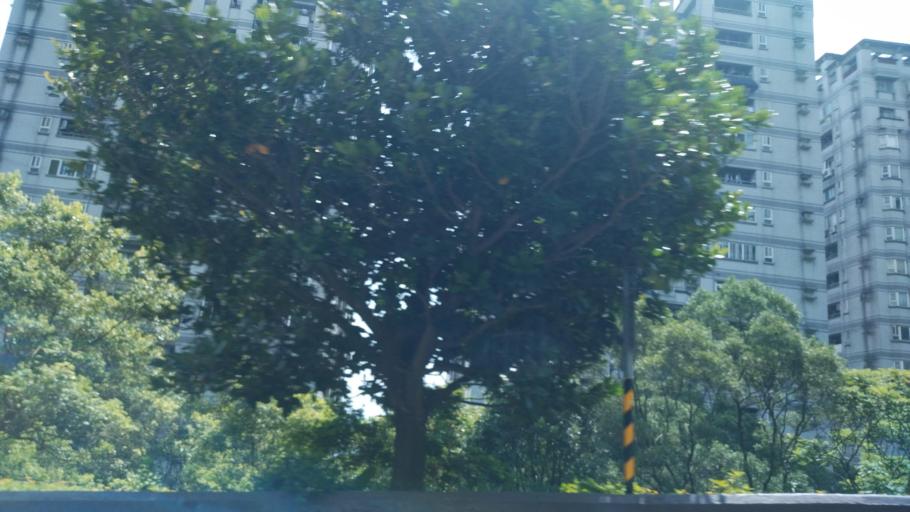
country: TW
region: Taipei
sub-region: Taipei
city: Banqiao
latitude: 24.9433
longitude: 121.5038
